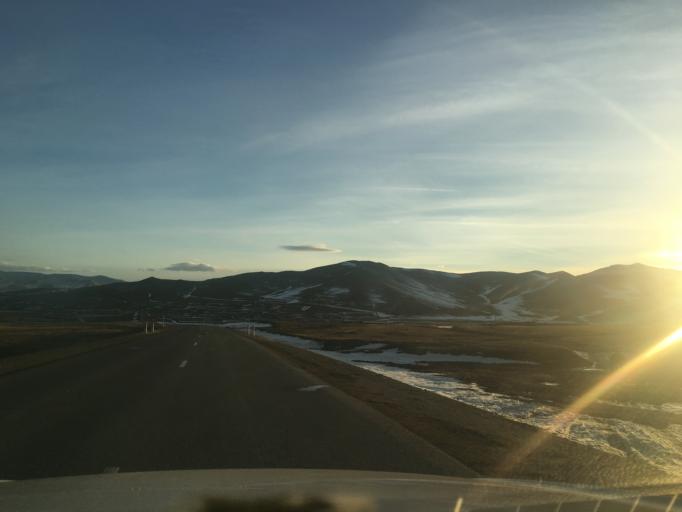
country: MN
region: Central Aimak
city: Mandal
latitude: 48.2117
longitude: 106.7083
